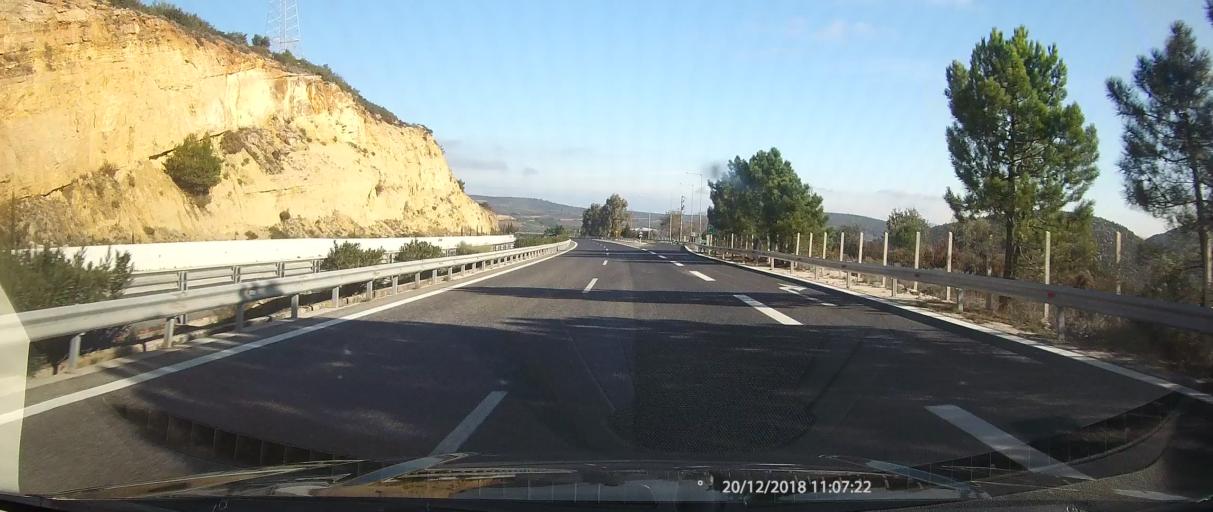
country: GR
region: Peloponnese
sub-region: Nomos Korinthias
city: Nemea
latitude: 37.7862
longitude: 22.7092
